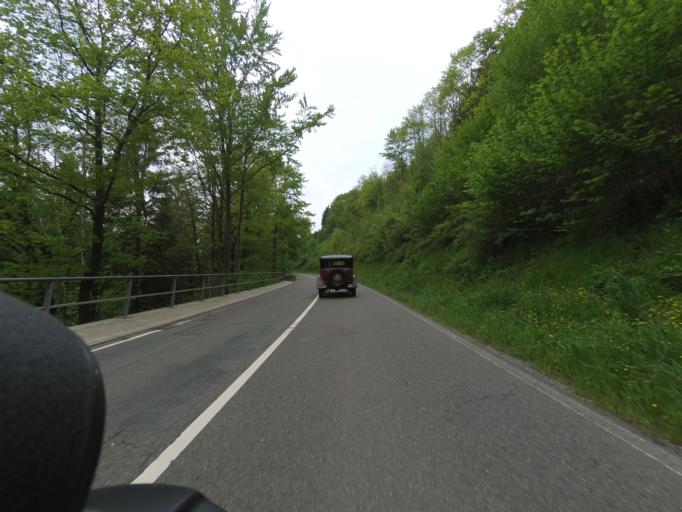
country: DE
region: Saxony
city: Scharfenstein
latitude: 50.7149
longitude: 13.0622
